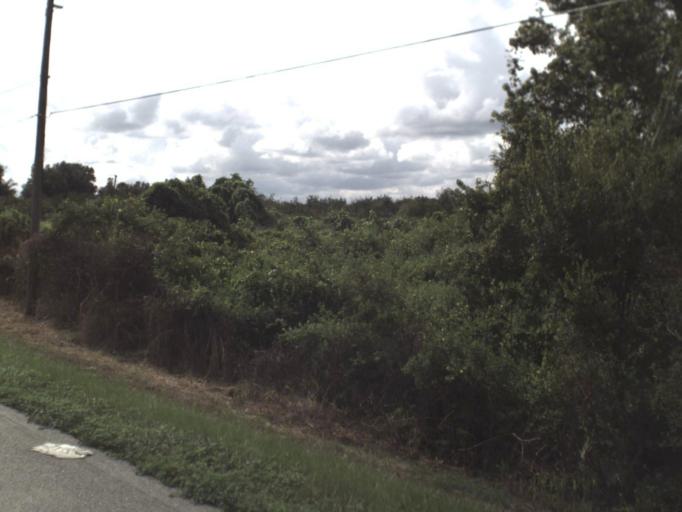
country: US
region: Florida
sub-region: DeSoto County
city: Arcadia
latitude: 27.2205
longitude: -81.8973
